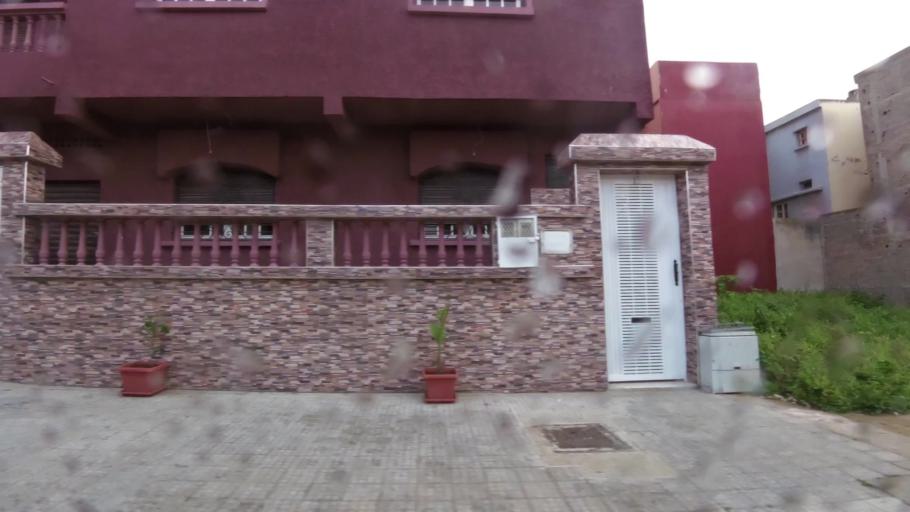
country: MA
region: Doukkala-Abda
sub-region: El-Jadida
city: El Jadida
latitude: 33.2498
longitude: -8.5250
